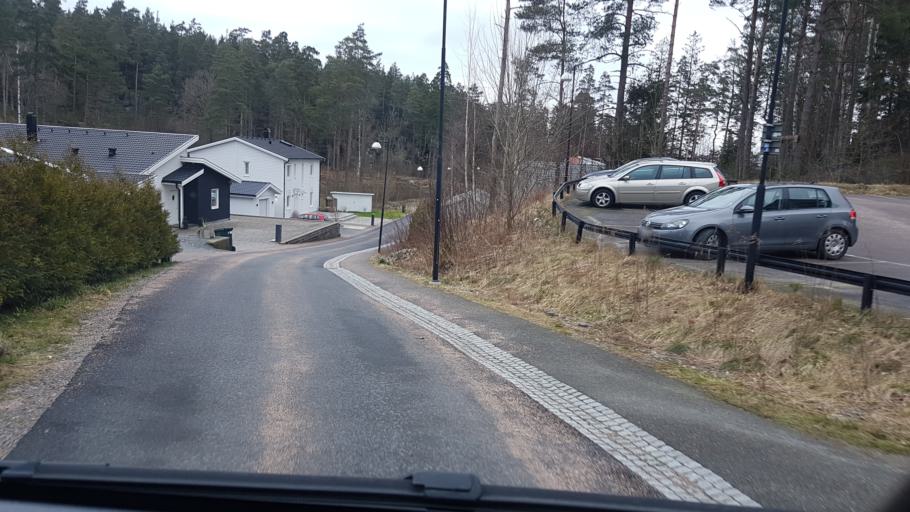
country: SE
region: Vaestra Goetaland
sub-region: Lerums Kommun
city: Lerum
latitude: 57.7837
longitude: 12.2715
